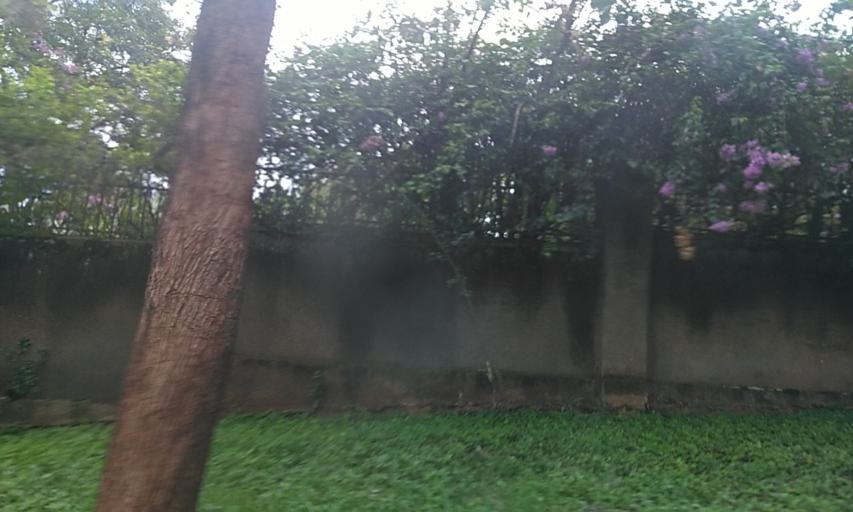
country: UG
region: Central Region
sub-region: Kampala District
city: Kampala
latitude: 0.3355
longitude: 32.5994
